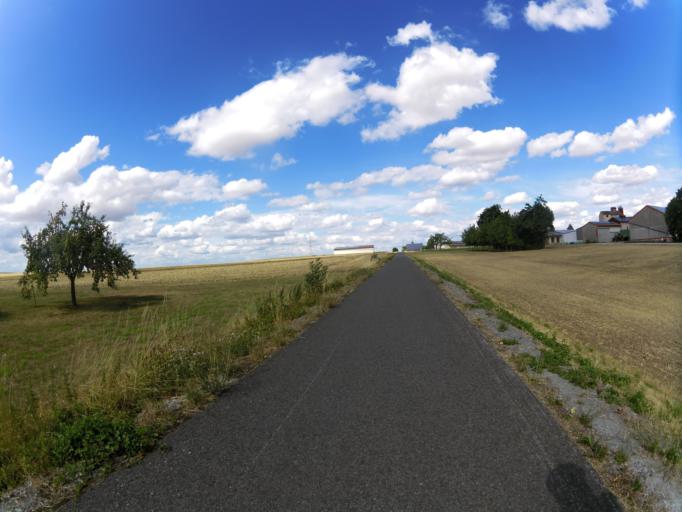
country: DE
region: Bavaria
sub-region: Regierungsbezirk Unterfranken
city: Sonderhofen
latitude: 49.6109
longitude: 10.0081
